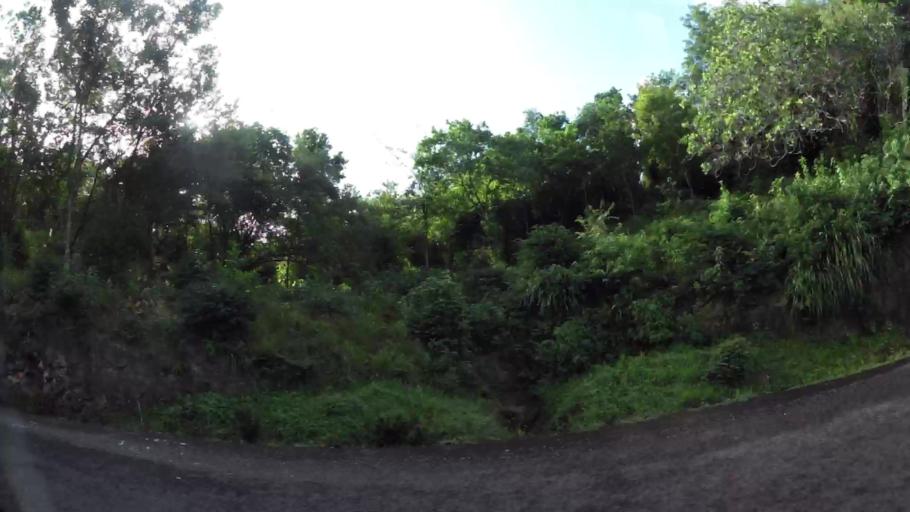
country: LC
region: Anse-la-Raye
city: Canaries
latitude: 13.8990
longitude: -61.0643
